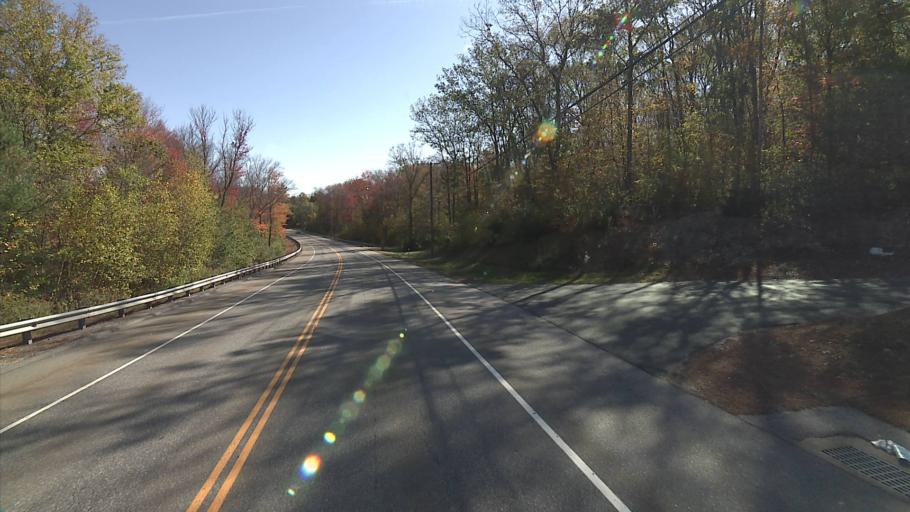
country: US
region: Connecticut
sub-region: Windham County
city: Wauregan
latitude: 41.7838
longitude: -71.9902
